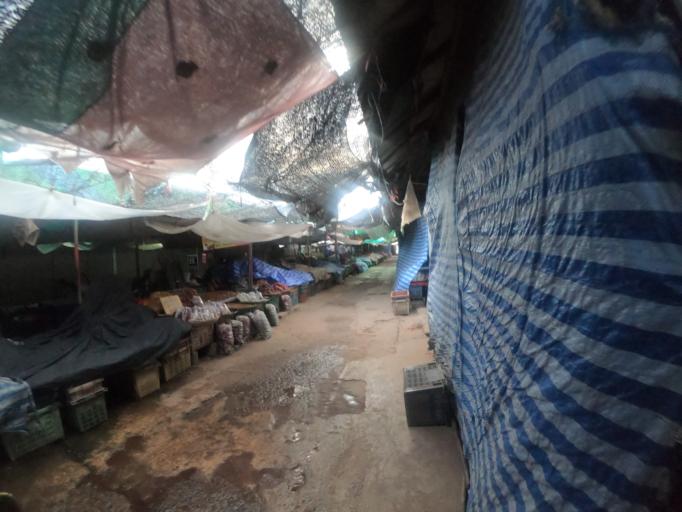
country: TH
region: Surin
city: Kap Choeng
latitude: 14.4542
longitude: 103.6877
